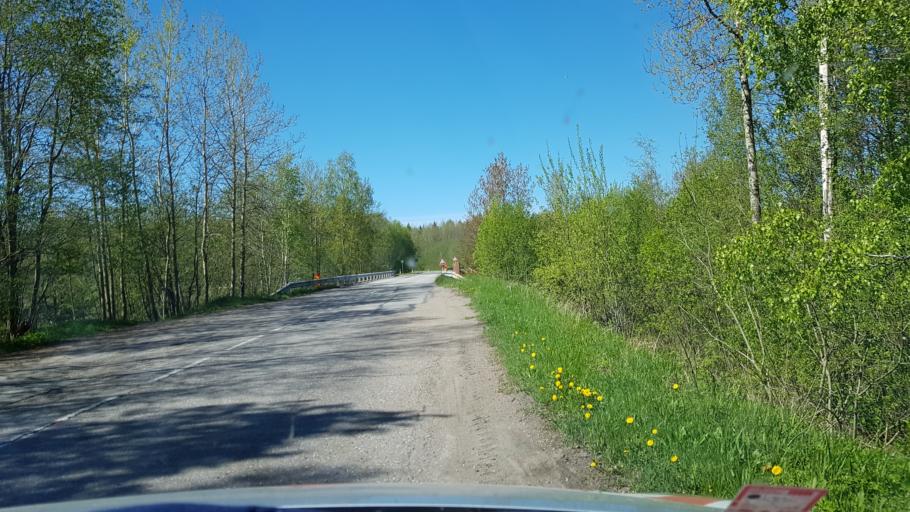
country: EE
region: Ida-Virumaa
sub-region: Narva linn
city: Narva
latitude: 59.3512
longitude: 28.0983
